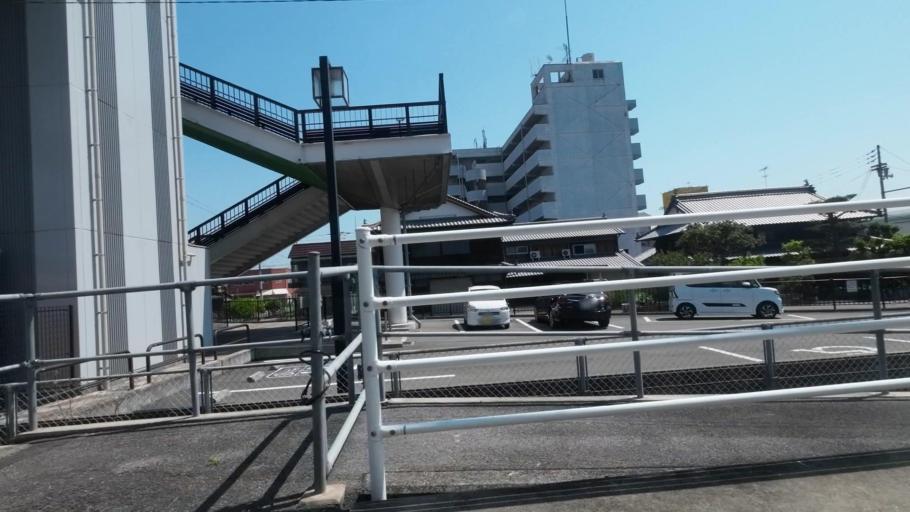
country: JP
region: Ehime
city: Saijo
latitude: 33.9292
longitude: 133.0860
